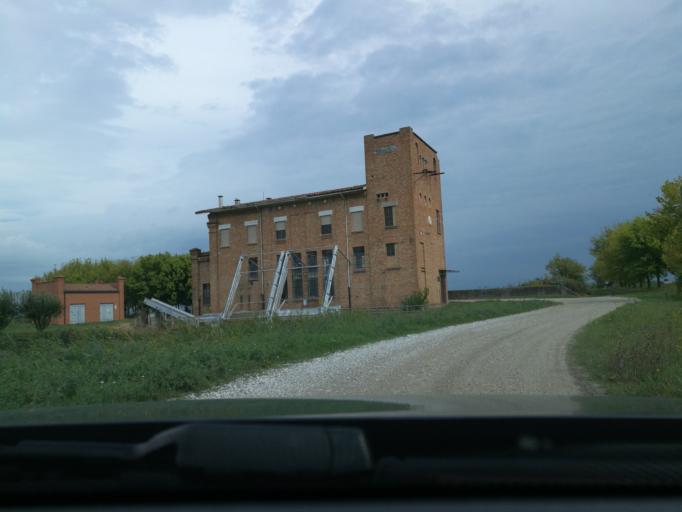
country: IT
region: Friuli Venezia Giulia
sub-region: Provincia di Udine
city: Pertegada
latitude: 45.7142
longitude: 13.0652
